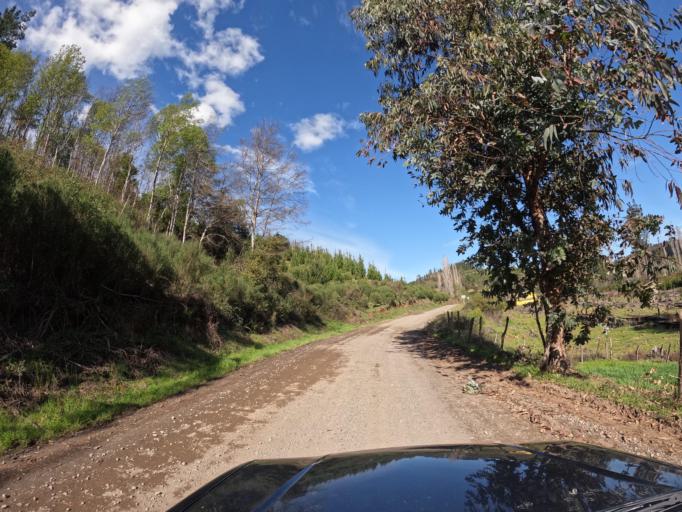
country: CL
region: Biobio
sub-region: Provincia de Concepcion
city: Chiguayante
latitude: -37.0680
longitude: -72.8488
